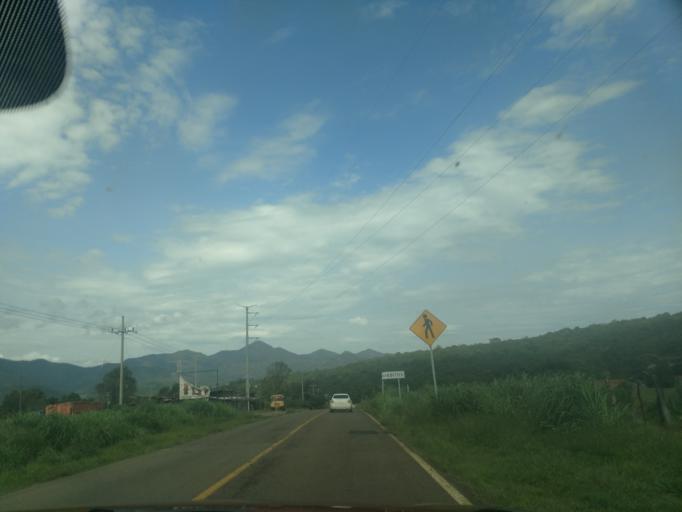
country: MX
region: Jalisco
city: Talpa de Allende
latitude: 20.4233
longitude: -104.7292
